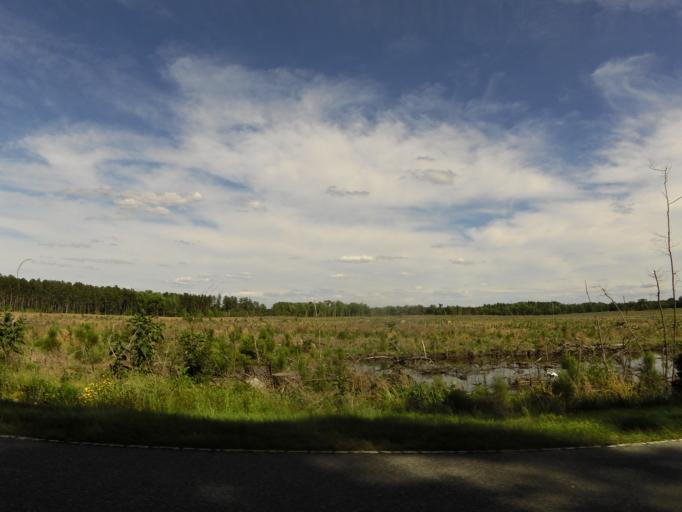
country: US
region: South Carolina
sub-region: Bamberg County
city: Denmark
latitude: 33.2426
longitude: -81.1674
